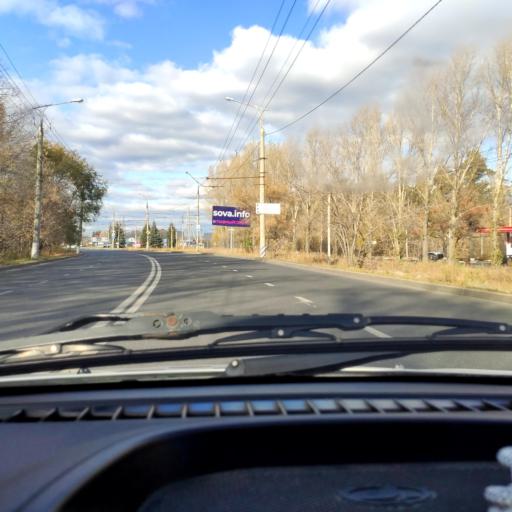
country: RU
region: Samara
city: Zhigulevsk
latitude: 53.5081
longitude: 49.4637
